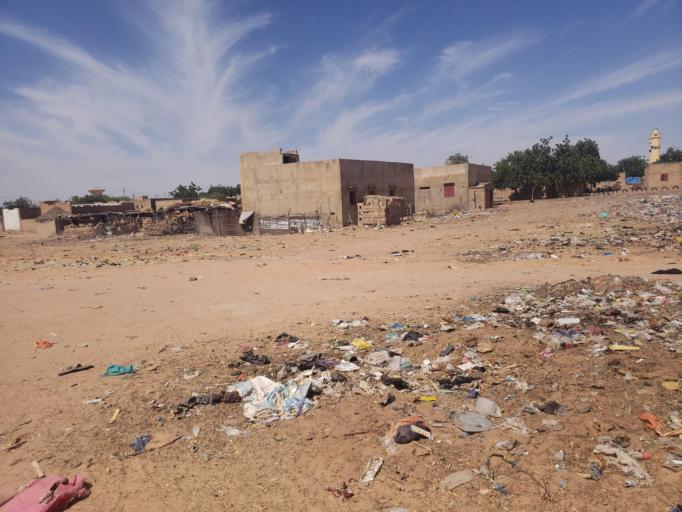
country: SN
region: Matam
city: Ranerou
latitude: 15.2970
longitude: -13.9594
